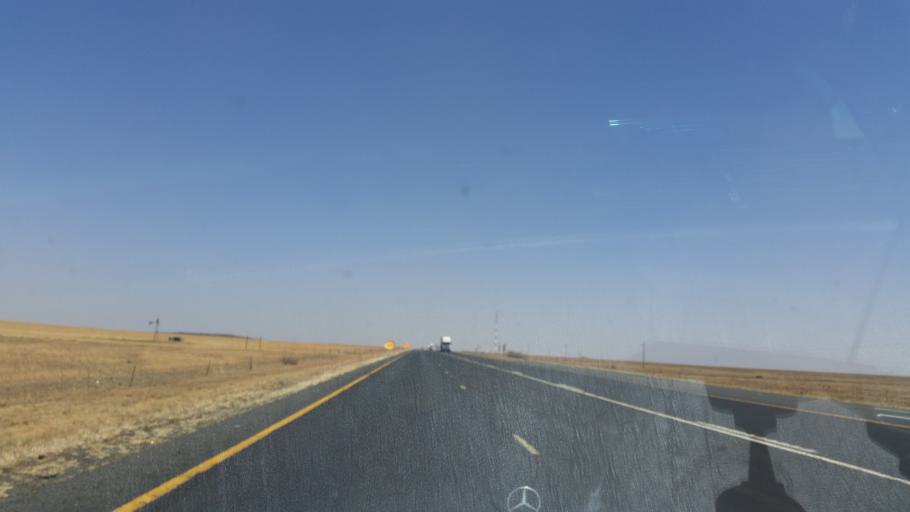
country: ZA
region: Orange Free State
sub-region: Lejweleputswa District Municipality
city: Brandfort
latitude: -28.8081
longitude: 26.6783
